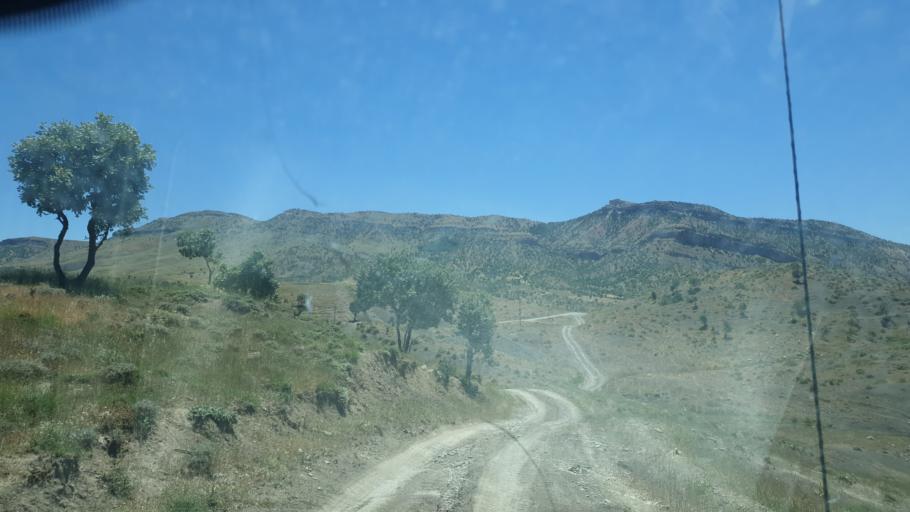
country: IQ
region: Arbil
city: Nahiyat Hiran
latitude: 36.2025
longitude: 44.4232
